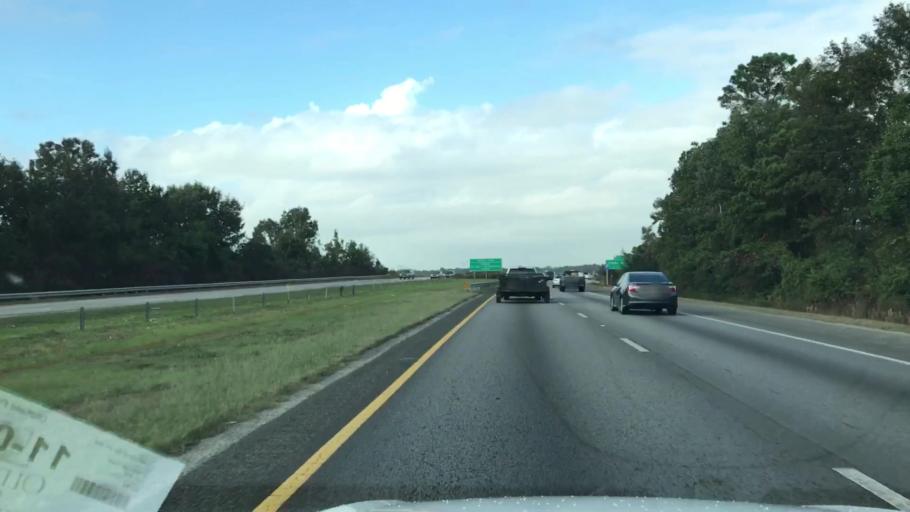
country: US
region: South Carolina
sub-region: Charleston County
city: North Charleston
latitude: 32.8273
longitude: -80.0297
